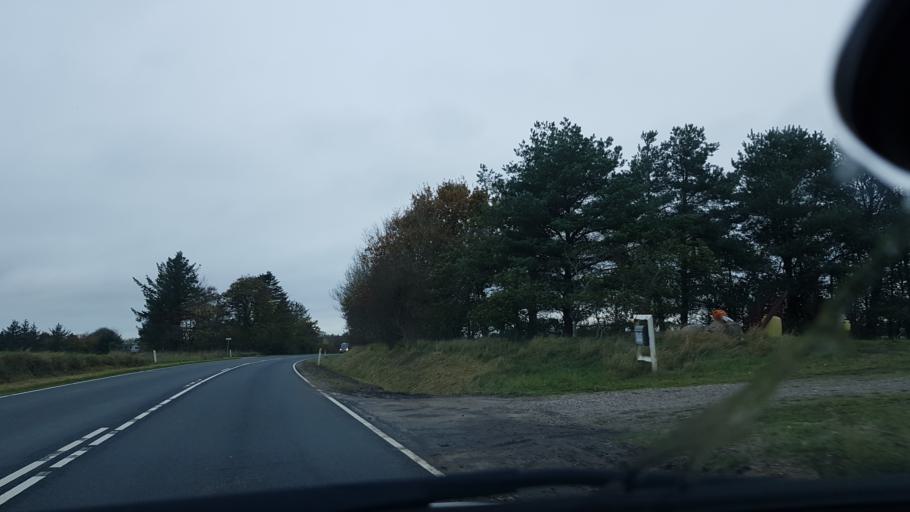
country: DK
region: South Denmark
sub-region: Esbjerg Kommune
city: Ribe
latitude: 55.2925
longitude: 8.8196
